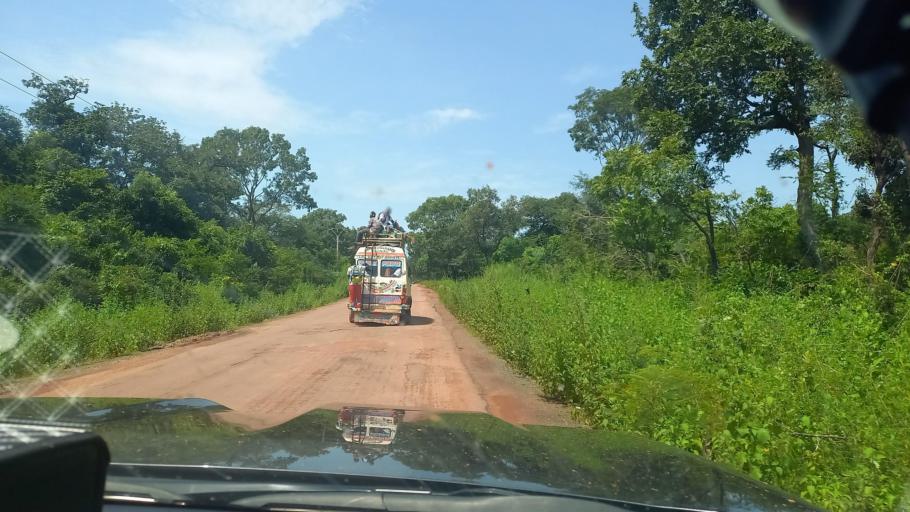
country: SN
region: Kolda
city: Marsassoum
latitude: 12.8576
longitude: -16.1018
